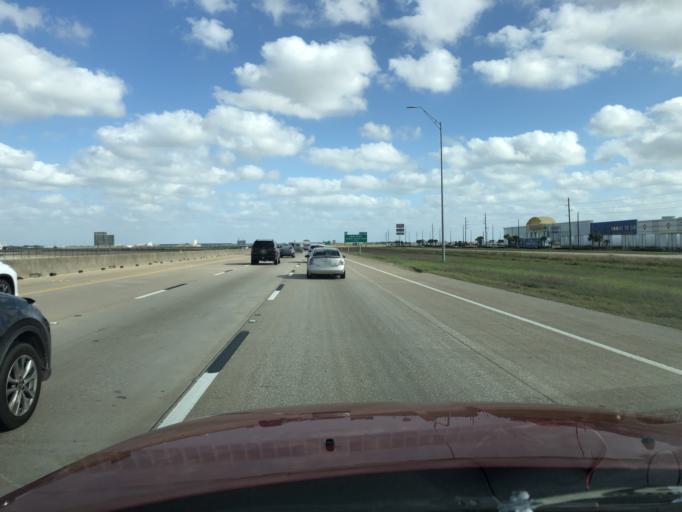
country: US
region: Texas
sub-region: Waller County
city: Brookshire
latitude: 29.7775
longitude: -95.9128
